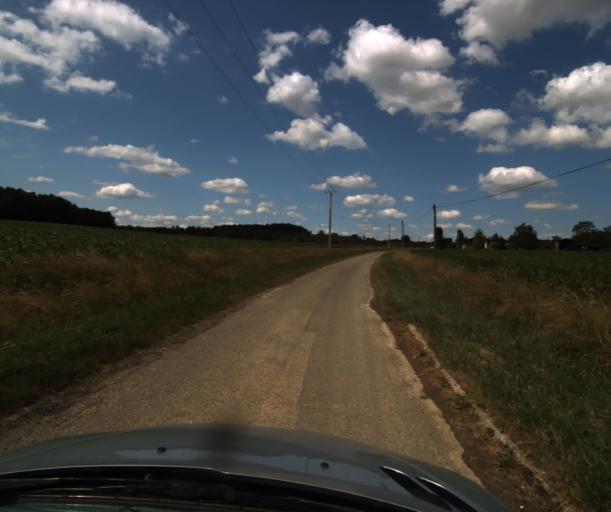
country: FR
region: Midi-Pyrenees
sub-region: Departement du Tarn-et-Garonne
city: Campsas
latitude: 43.9178
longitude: 1.2978
